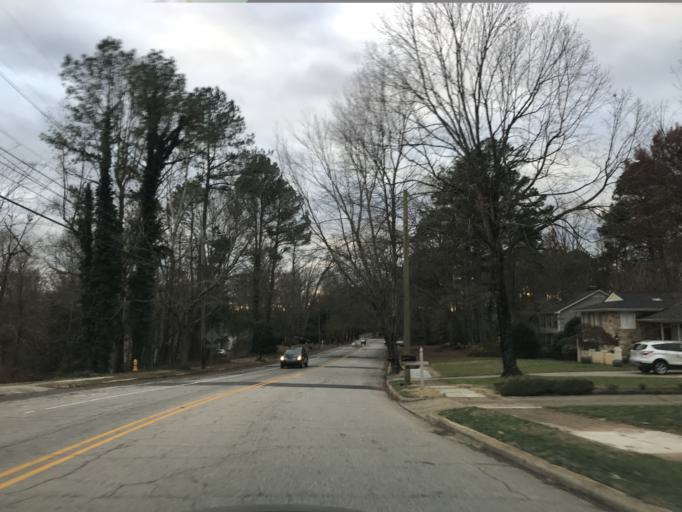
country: US
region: North Carolina
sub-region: Wake County
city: West Raleigh
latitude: 35.8523
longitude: -78.6585
